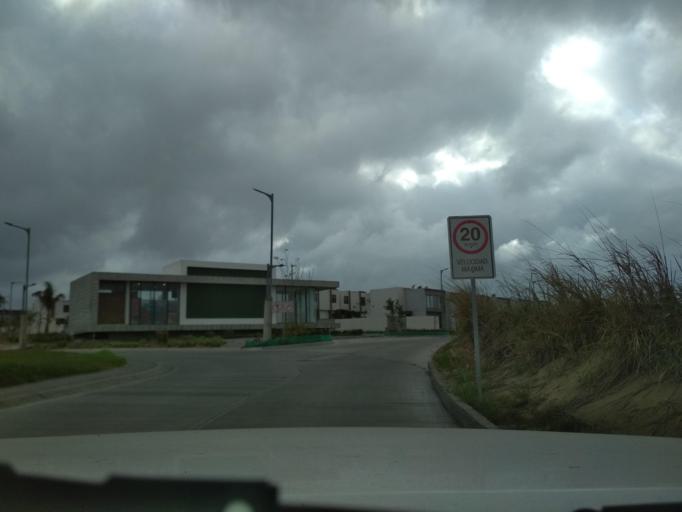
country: MX
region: Veracruz
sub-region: Veracruz
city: Fraccionamiento Geovillas los Pinos
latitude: 19.2177
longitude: -96.2316
